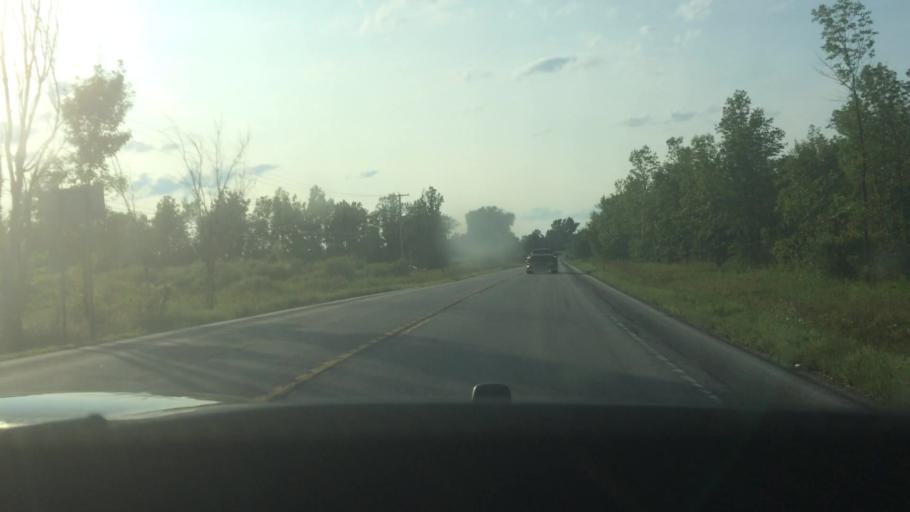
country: US
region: New York
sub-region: St. Lawrence County
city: Ogdensburg
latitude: 44.6733
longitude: -75.4321
